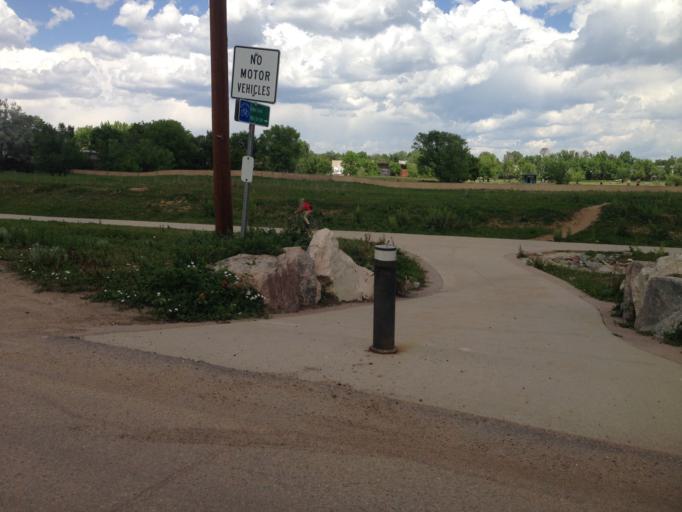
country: US
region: Colorado
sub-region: Boulder County
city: Boulder
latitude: 40.0256
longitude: -105.2384
